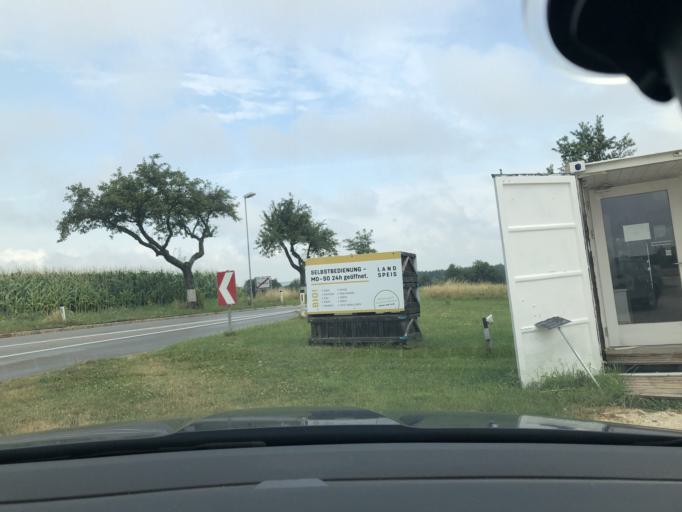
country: AT
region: Lower Austria
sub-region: Politischer Bezirk Mistelbach
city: Hochleithen
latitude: 48.5025
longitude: 16.5215
